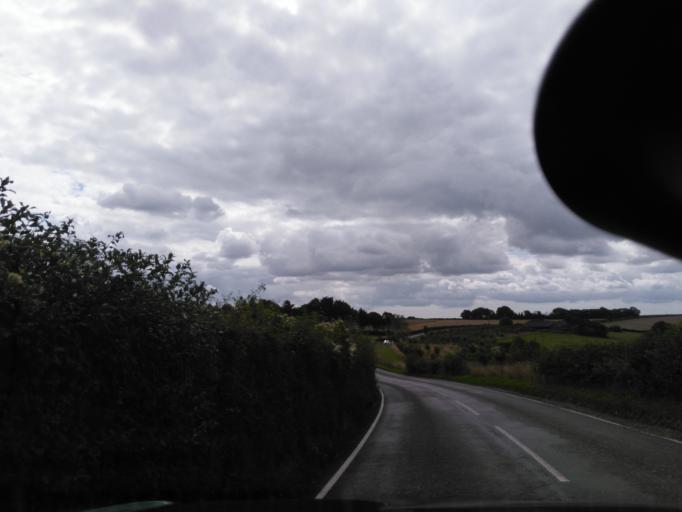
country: GB
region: England
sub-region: Dorset
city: Blandford Forum
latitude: 50.9041
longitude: -2.1575
